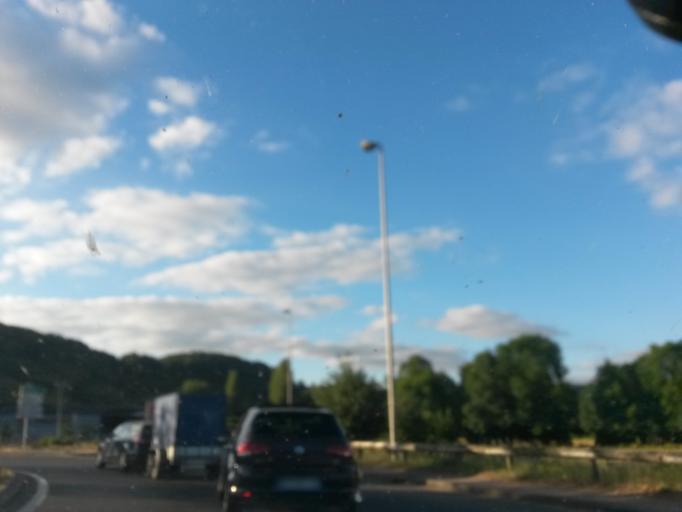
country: FR
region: Bourgogne
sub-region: Departement de la Nievre
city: Premery
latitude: 47.1738
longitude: 3.3272
